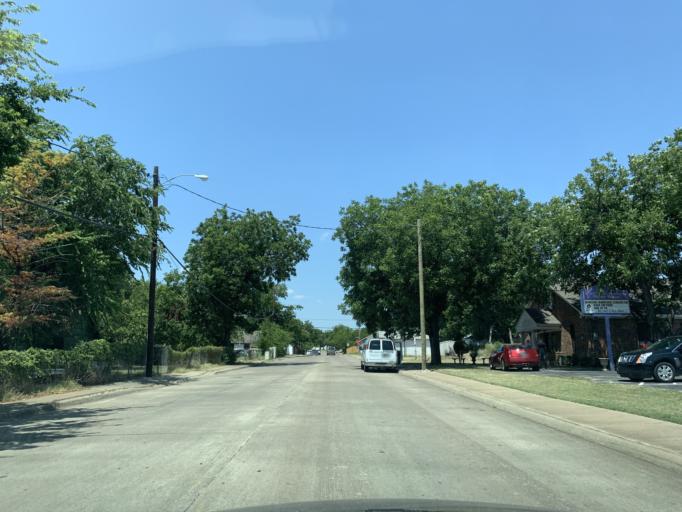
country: US
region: Texas
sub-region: Dallas County
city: Dallas
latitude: 32.6924
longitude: -96.8019
